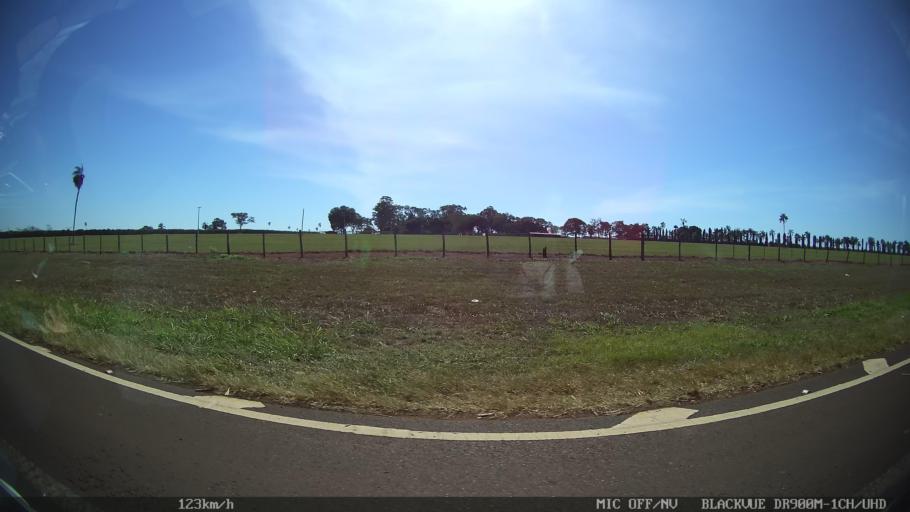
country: BR
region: Sao Paulo
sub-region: Barretos
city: Barretos
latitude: -20.5690
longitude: -48.6677
